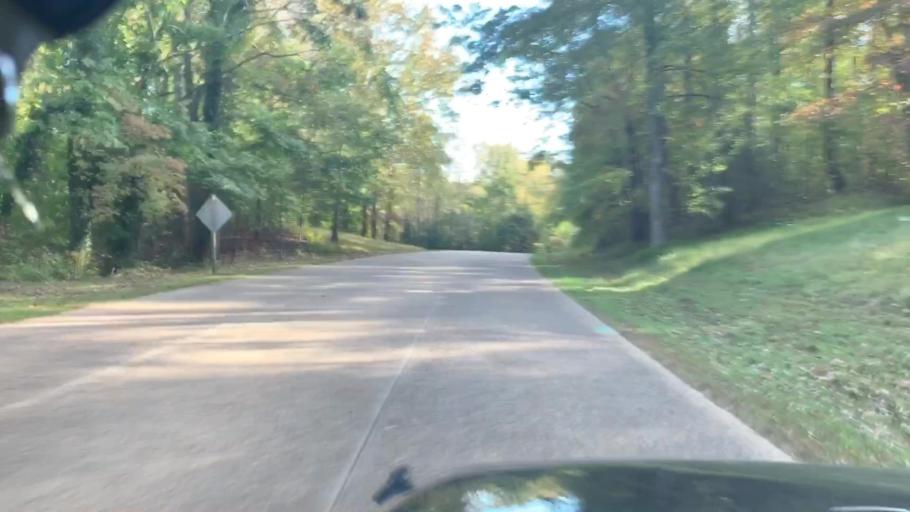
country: US
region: Virginia
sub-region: City of Williamsburg
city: Williamsburg
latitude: 37.2611
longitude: -76.7021
